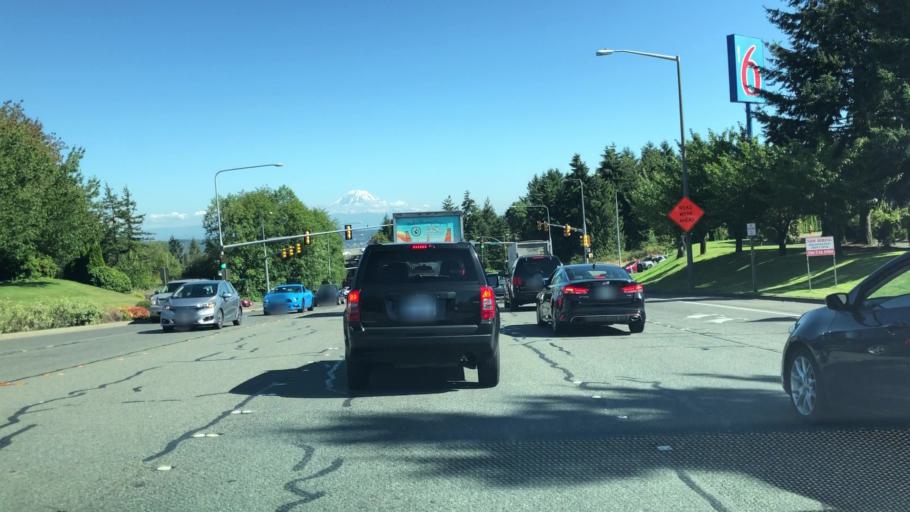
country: US
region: Washington
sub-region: King County
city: SeaTac
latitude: 47.4337
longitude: -122.2739
